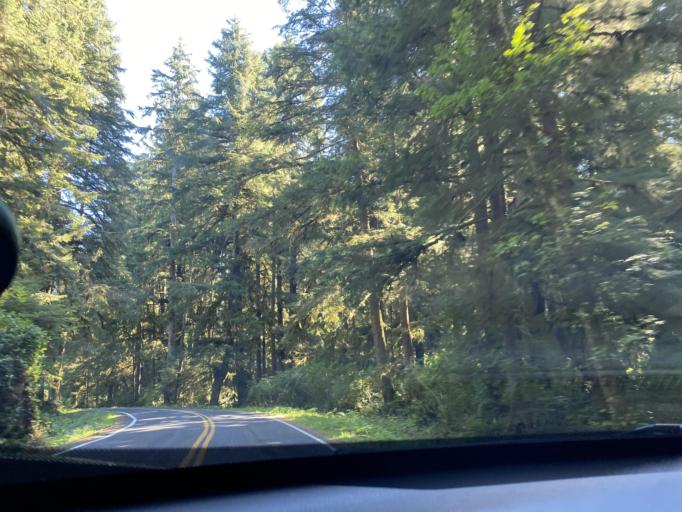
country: US
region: Washington
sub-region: Clallam County
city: Forks
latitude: 47.9195
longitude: -124.6098
